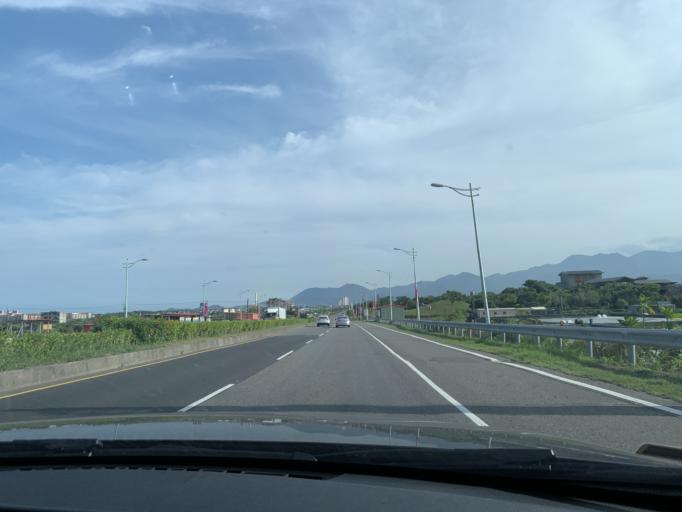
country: TW
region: Taiwan
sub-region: Yilan
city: Yilan
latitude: 24.6907
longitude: 121.8250
